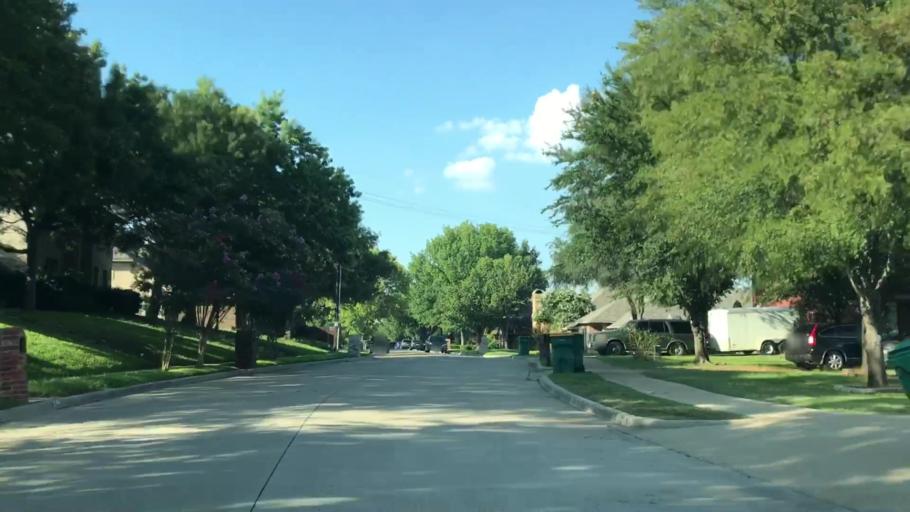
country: US
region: Texas
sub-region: Denton County
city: Lewisville
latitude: 33.0099
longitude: -97.0112
